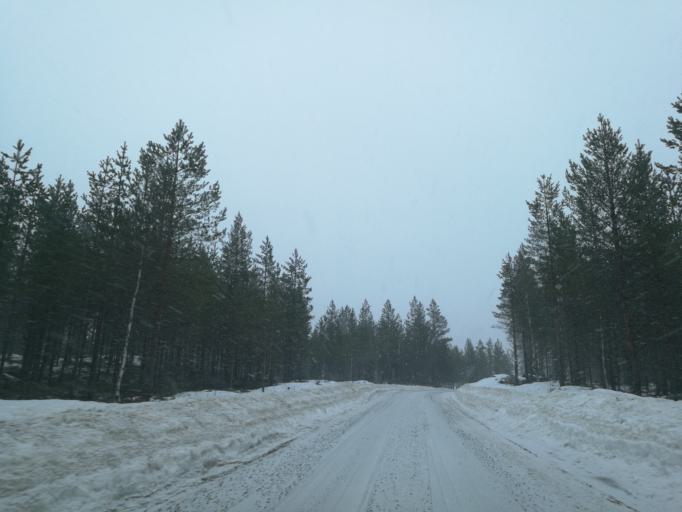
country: SE
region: Vaermland
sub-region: Torsby Kommun
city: Torsby
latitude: 60.6442
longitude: 12.7791
